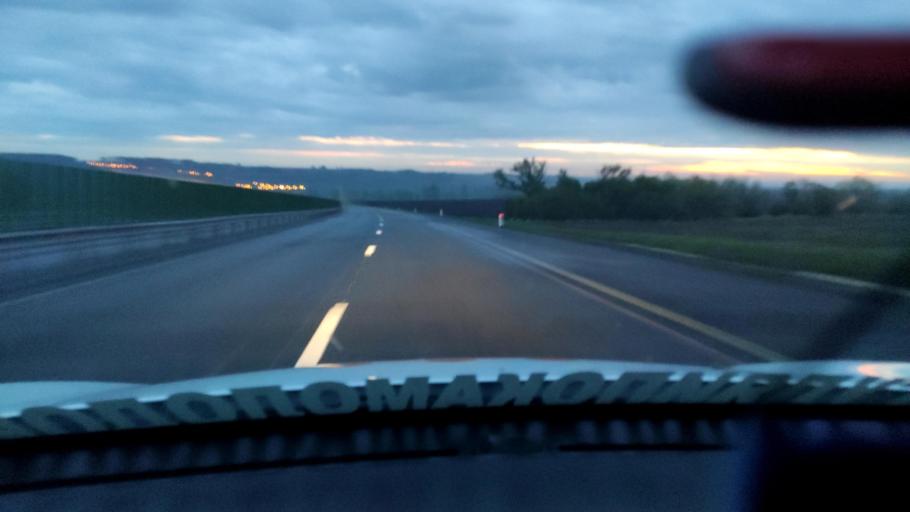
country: RU
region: Rostov
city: Tarasovskiy
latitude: 48.7193
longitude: 40.4039
